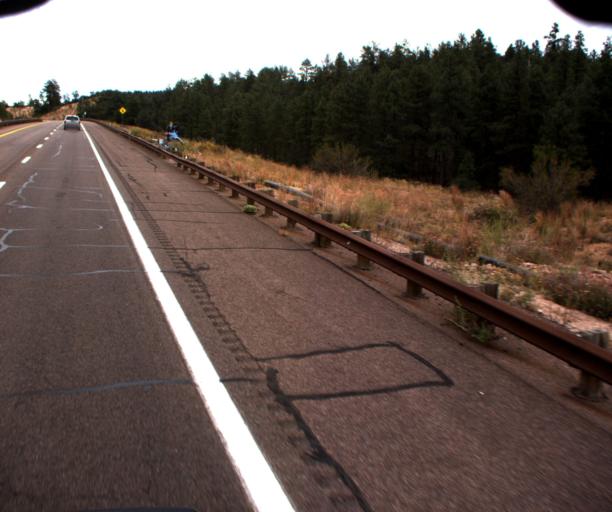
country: US
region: Arizona
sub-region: Gila County
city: Star Valley
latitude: 34.2783
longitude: -111.1624
